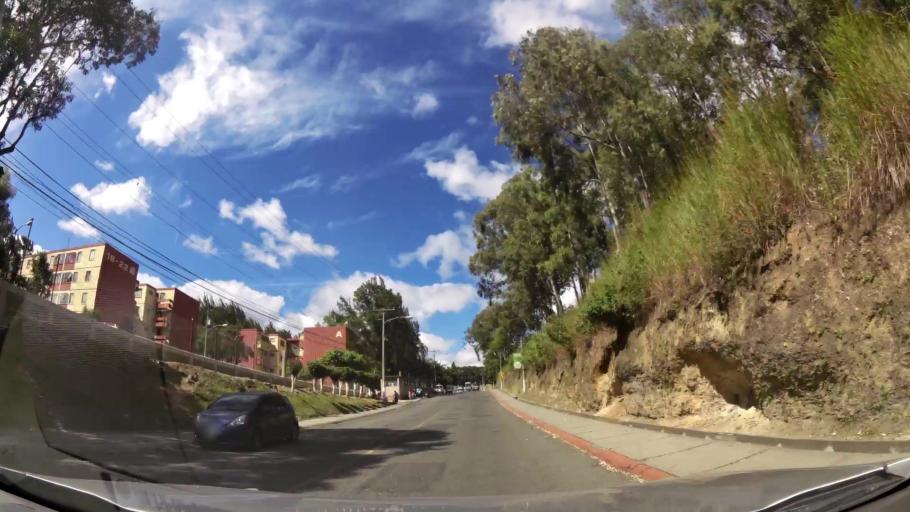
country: GT
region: Guatemala
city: Villa Nueva
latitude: 14.5443
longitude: -90.5511
